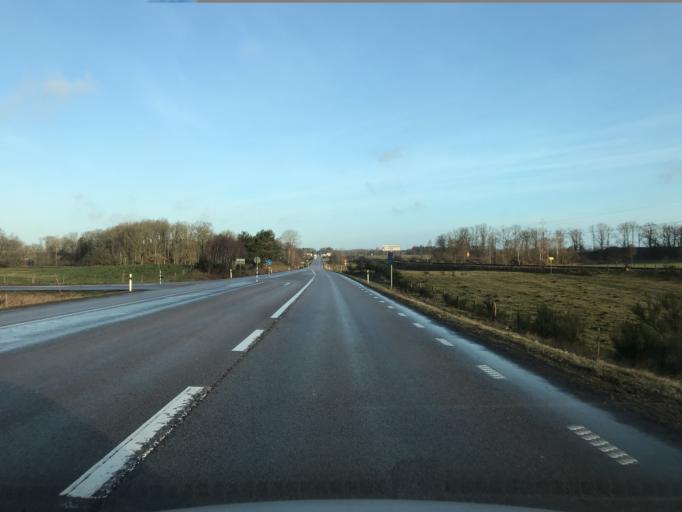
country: SE
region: Skane
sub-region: Hassleholms Kommun
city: Hassleholm
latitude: 56.1871
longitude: 13.7527
